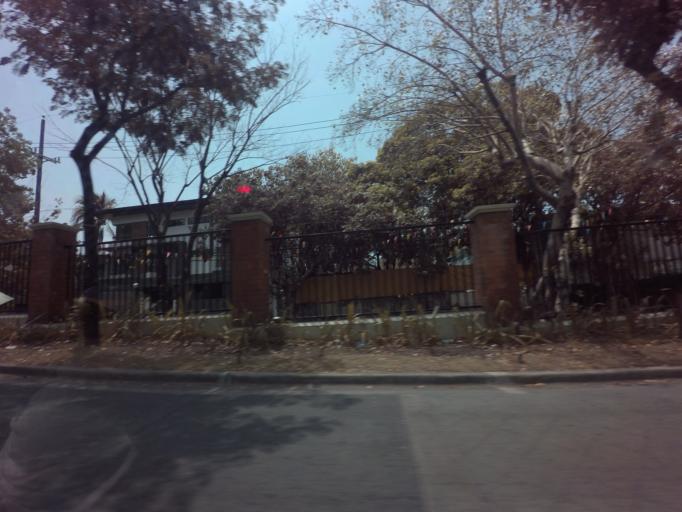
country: PH
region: Metro Manila
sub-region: Makati City
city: Makati City
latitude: 14.5620
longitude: 121.0332
